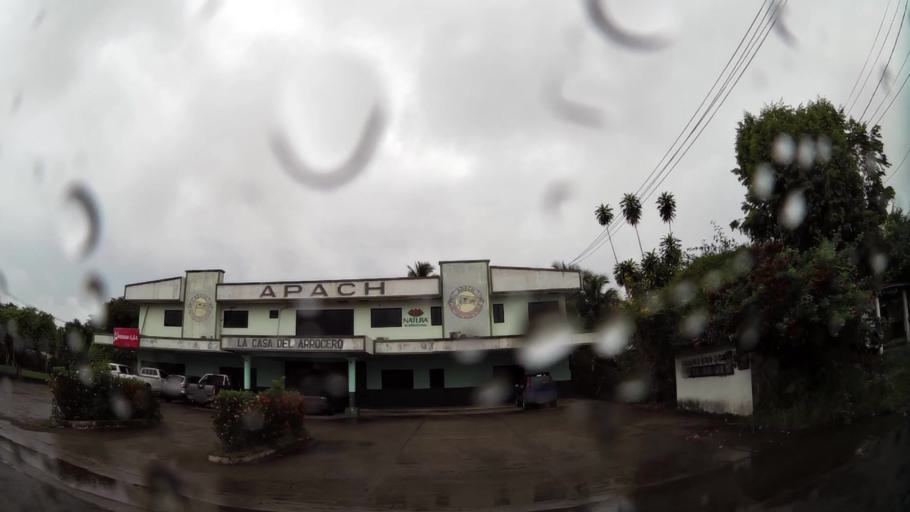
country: PA
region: Chiriqui
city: David
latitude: 8.4325
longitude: -82.4364
